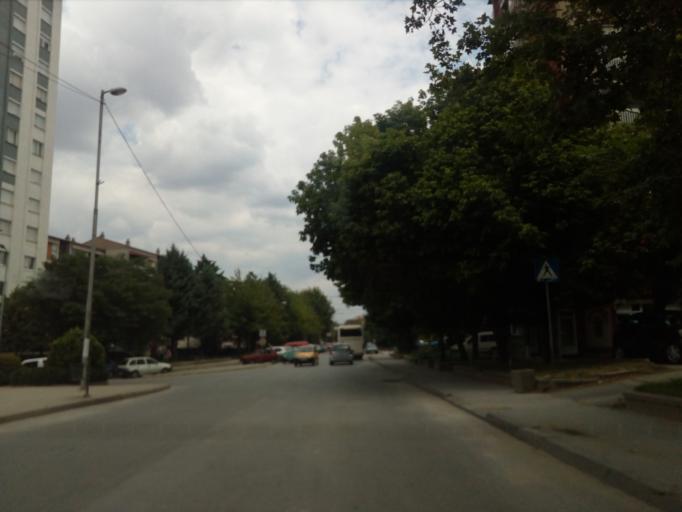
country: MK
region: Veles
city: Veles
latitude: 41.7136
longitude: 21.7660
